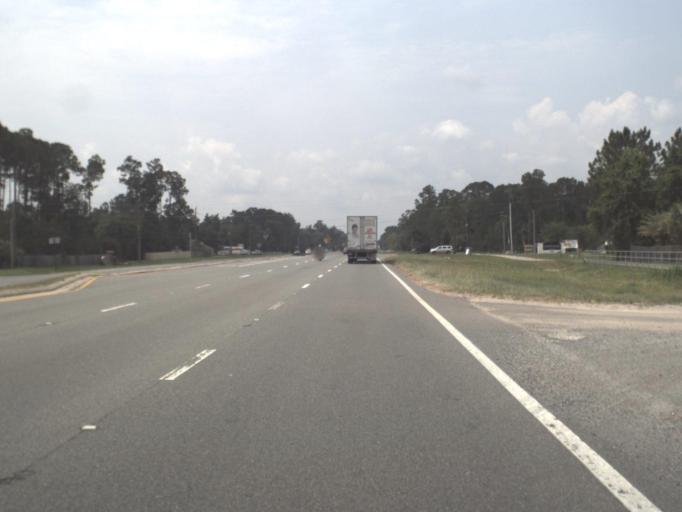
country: US
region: Florida
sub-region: Clay County
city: Green Cove Springs
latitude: 30.0647
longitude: -81.7076
